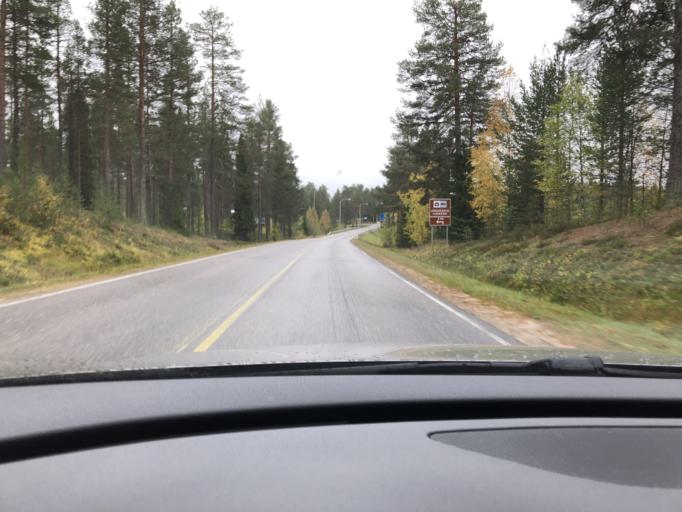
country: FI
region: Lapland
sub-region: Itae-Lappi
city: Posio
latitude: 66.1161
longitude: 28.1824
